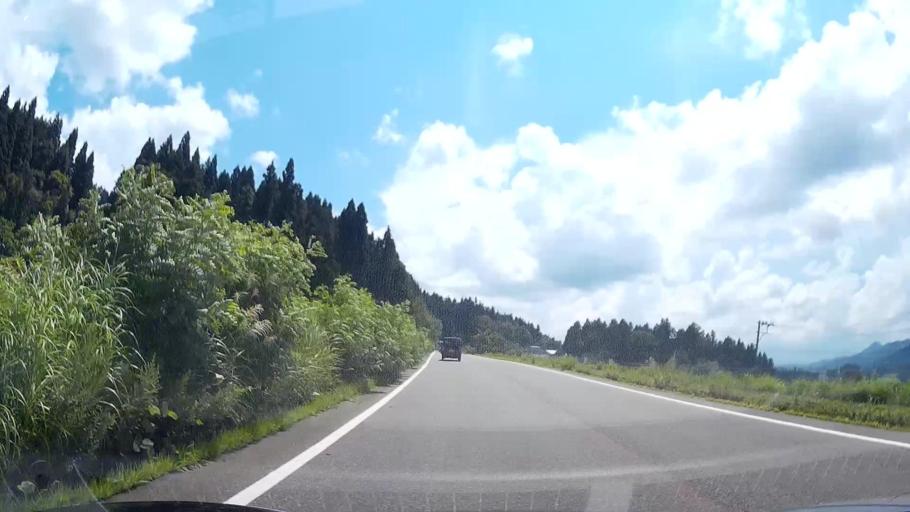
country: JP
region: Niigata
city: Tokamachi
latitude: 37.0687
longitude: 138.7135
